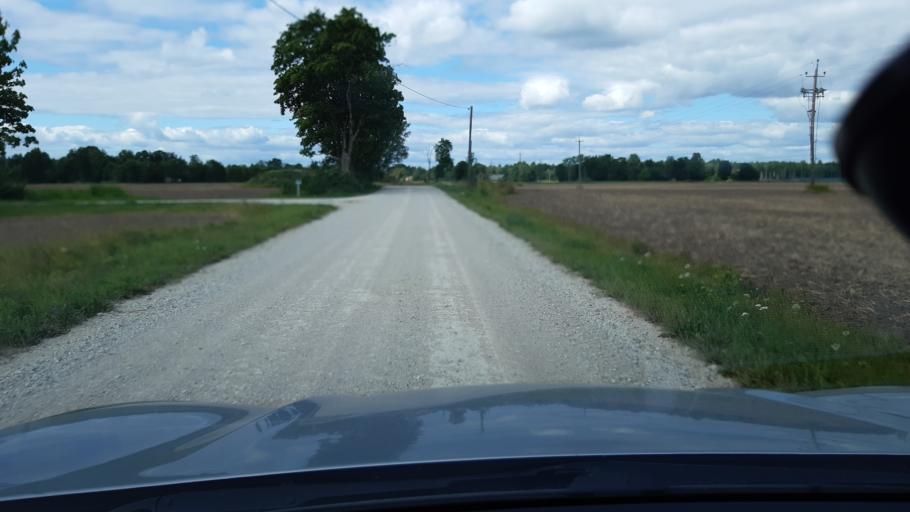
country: EE
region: Paernumaa
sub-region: Vaendra vald (alev)
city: Vandra
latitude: 58.7915
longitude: 25.0133
